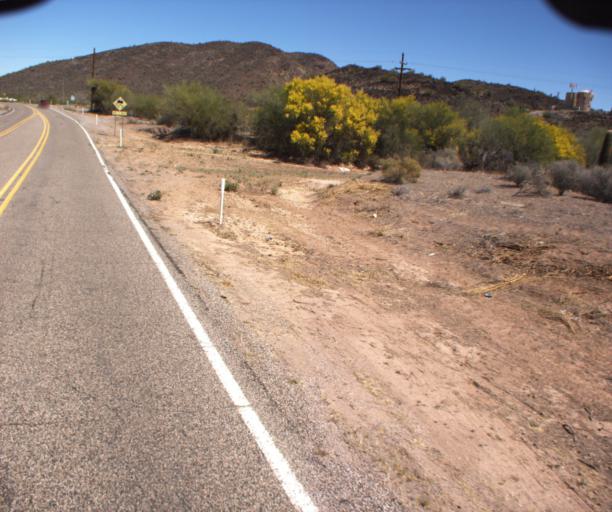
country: US
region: Arizona
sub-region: Pima County
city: Ajo
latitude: 32.2661
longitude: -112.7395
